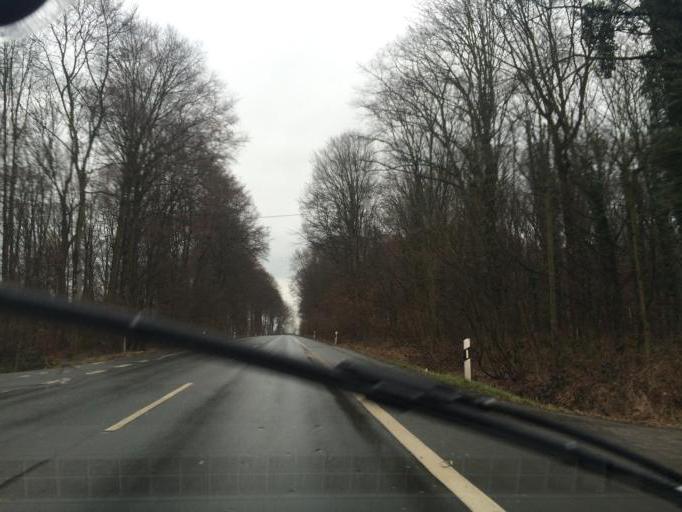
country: DE
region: North Rhine-Westphalia
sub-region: Regierungsbezirk Munster
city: Gladbeck
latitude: 51.6018
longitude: 6.9619
